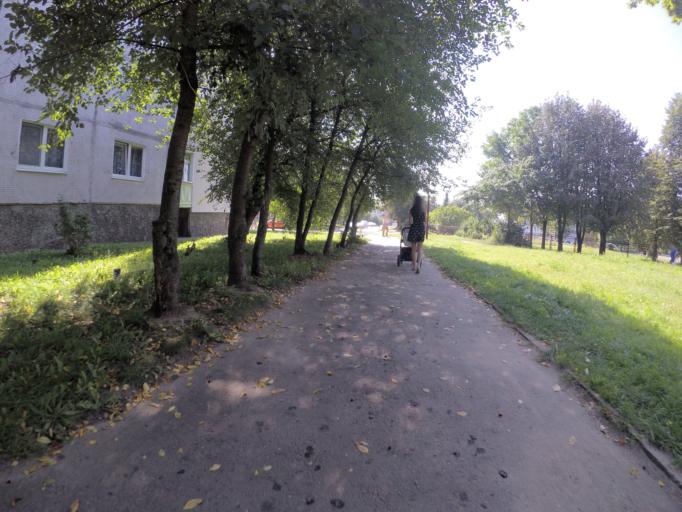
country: BY
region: Grodnenskaya
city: Hrodna
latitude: 53.7039
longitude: 23.8459
